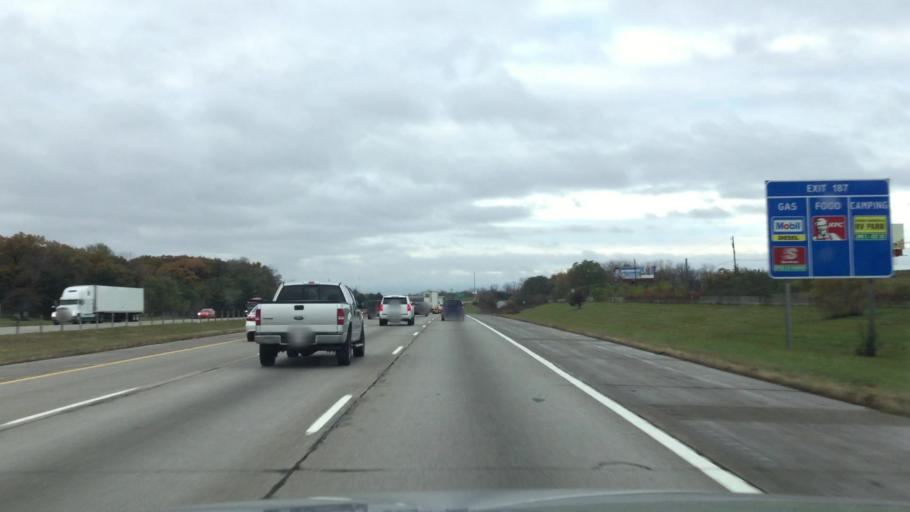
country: US
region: Michigan
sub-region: Wayne County
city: Belleville
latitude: 42.2191
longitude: -83.5305
